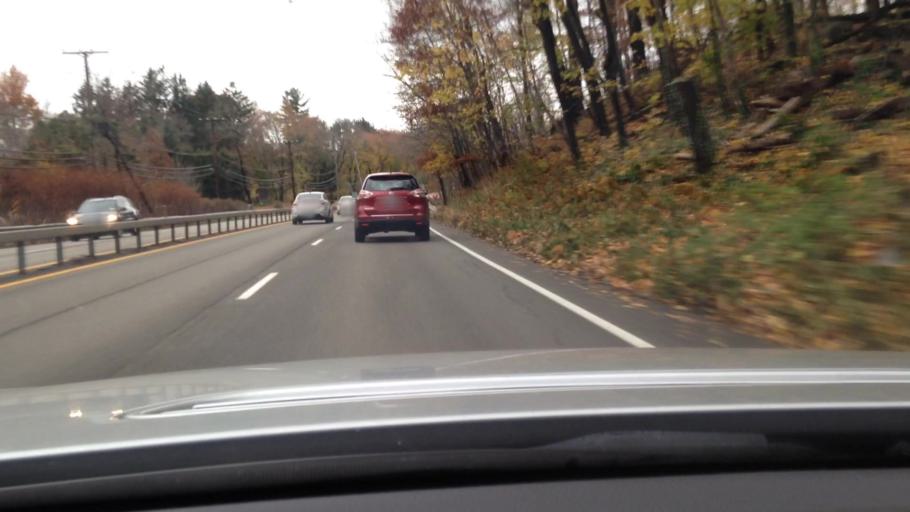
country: US
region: New York
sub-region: Westchester County
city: Briarcliff Manor
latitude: 41.1563
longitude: -73.8345
